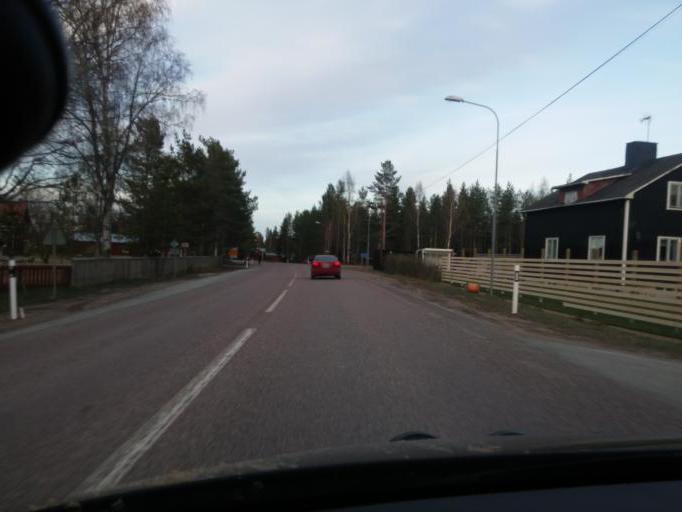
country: SE
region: Gaevleborg
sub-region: Ljusdals Kommun
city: Ljusdal
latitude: 61.8347
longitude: 16.0175
